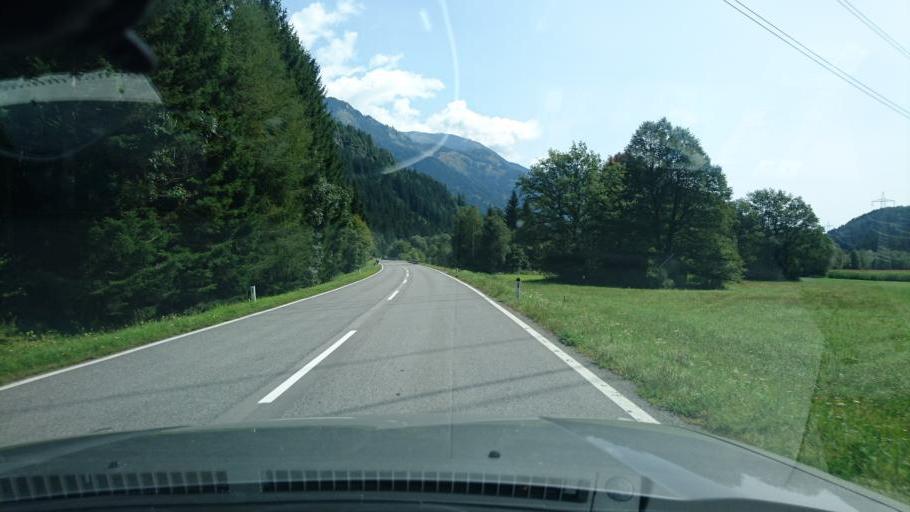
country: AT
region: Carinthia
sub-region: Politischer Bezirk Spittal an der Drau
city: Muhldorf
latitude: 46.8822
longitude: 13.2777
